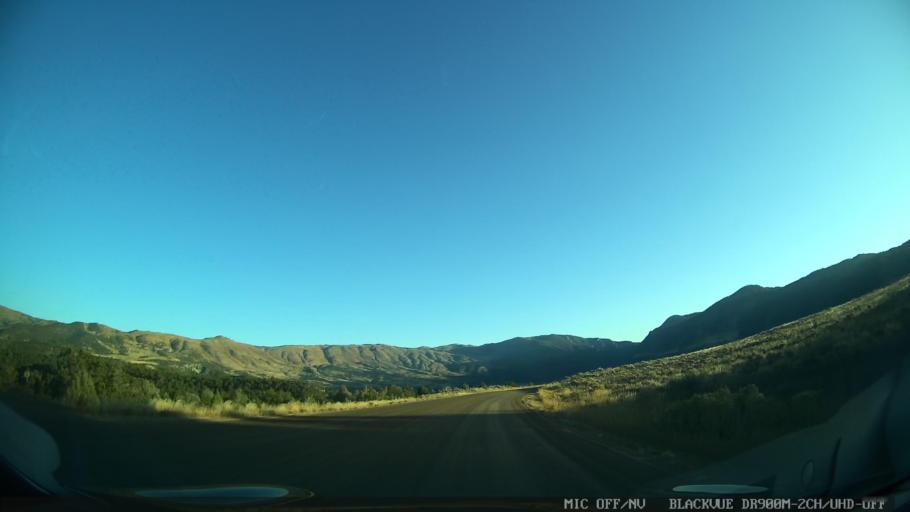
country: US
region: Colorado
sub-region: Grand County
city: Kremmling
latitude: 39.9647
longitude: -106.5208
